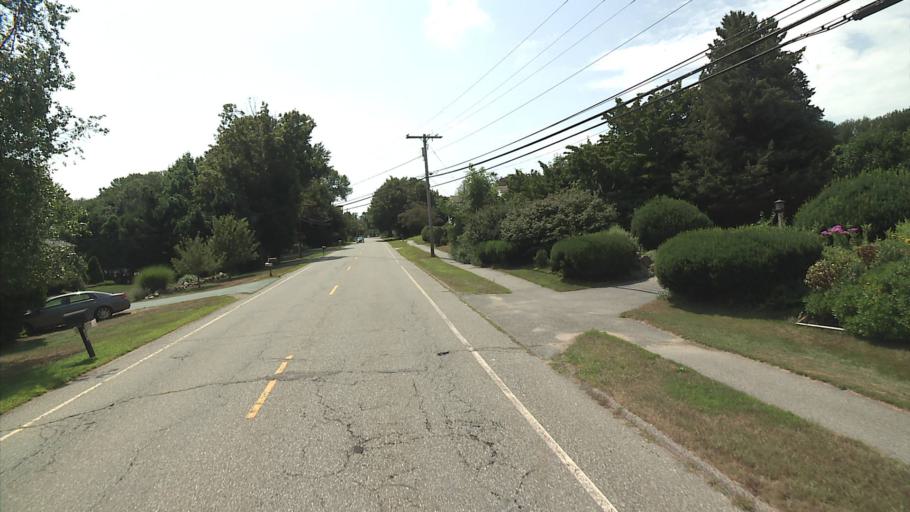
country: US
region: Connecticut
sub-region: New London County
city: Central Waterford
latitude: 41.3210
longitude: -72.1337
